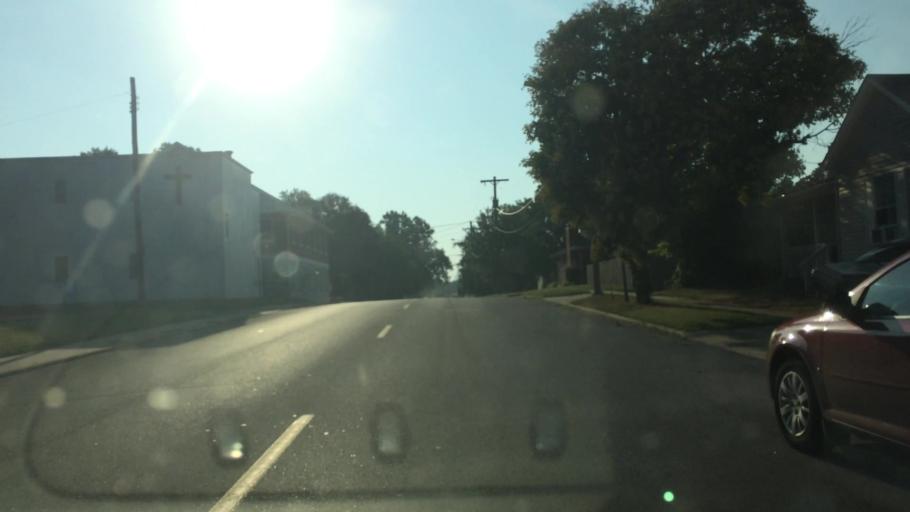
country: US
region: Missouri
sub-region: Greene County
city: Springfield
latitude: 37.2186
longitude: -93.2735
